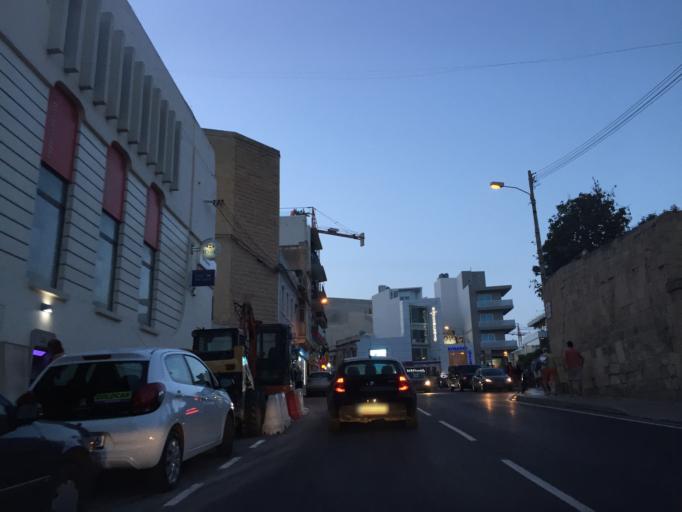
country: MT
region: Saint Julian
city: San Giljan
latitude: 35.9206
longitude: 14.4906
